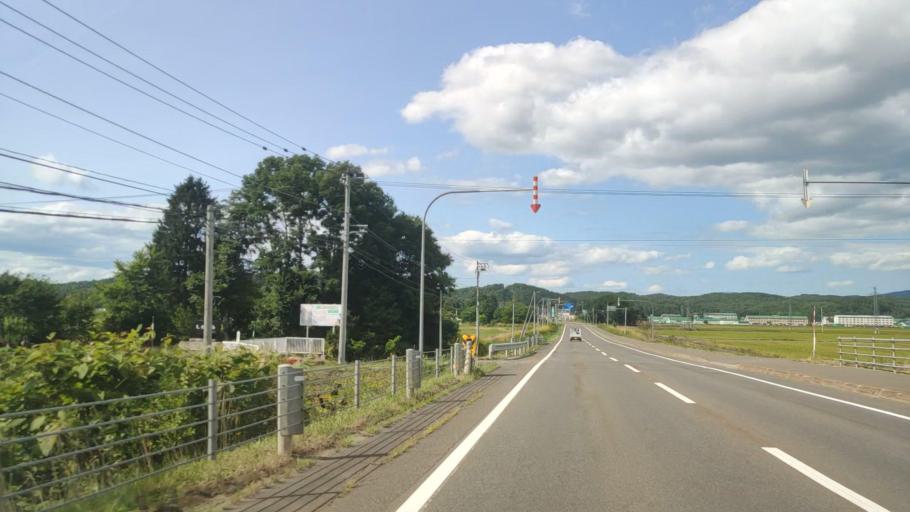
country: JP
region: Hokkaido
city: Nayoro
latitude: 44.3737
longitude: 142.4361
